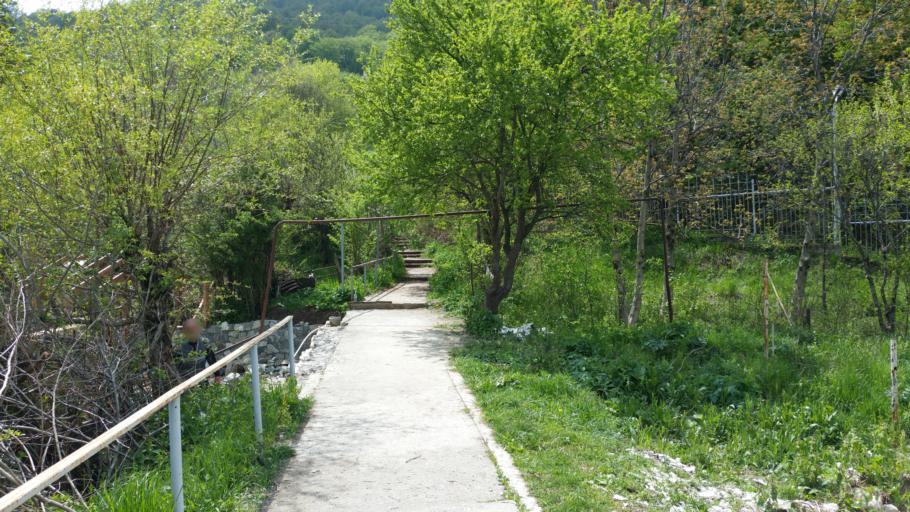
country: AM
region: Tavush
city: Dilijan
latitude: 40.7390
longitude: 44.8427
